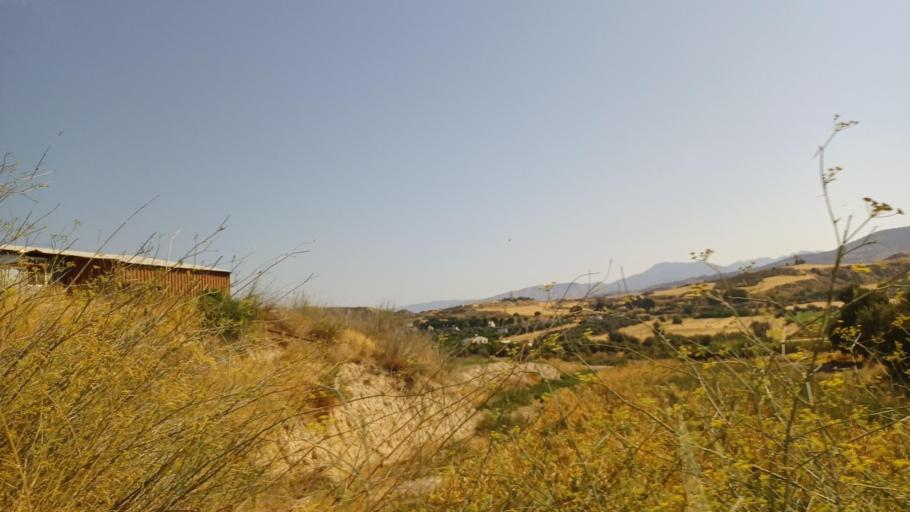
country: CY
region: Pafos
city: Polis
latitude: 35.0104
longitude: 32.4277
